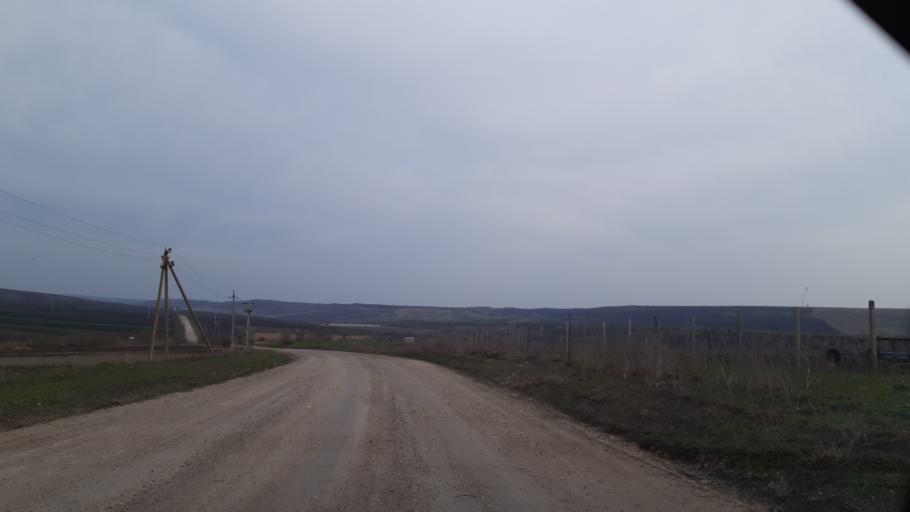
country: MD
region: Soldanesti
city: Soldanesti
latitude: 47.7079
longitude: 28.7102
